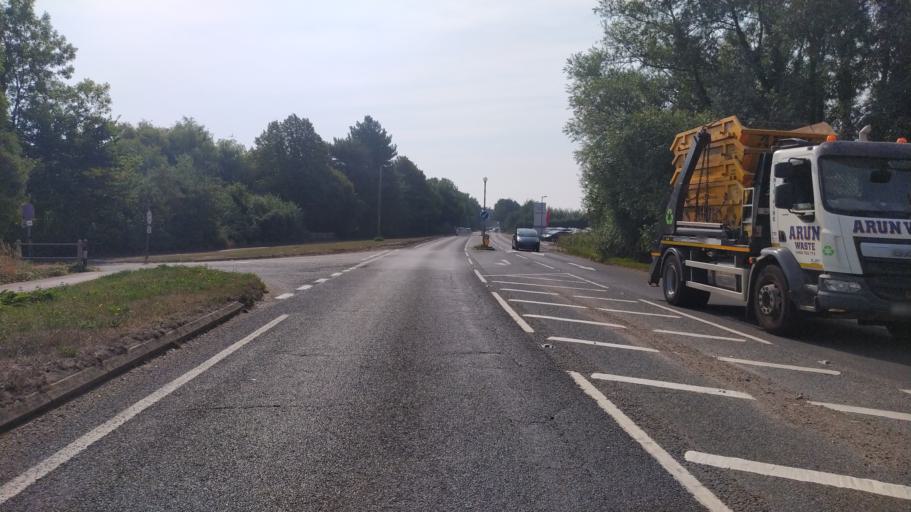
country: GB
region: England
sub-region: West Sussex
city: Bognor Regis
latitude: 50.8121
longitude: -0.7069
